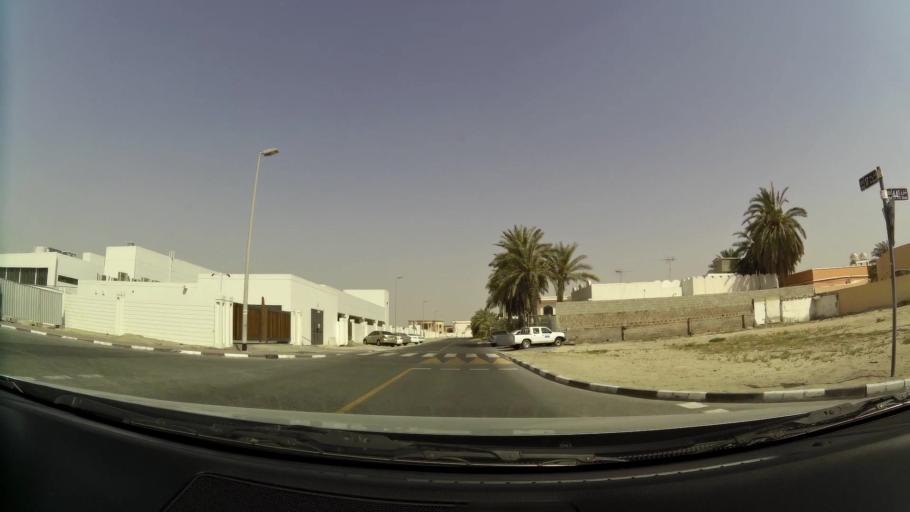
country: AE
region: Dubai
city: Dubai
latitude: 25.1666
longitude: 55.2577
